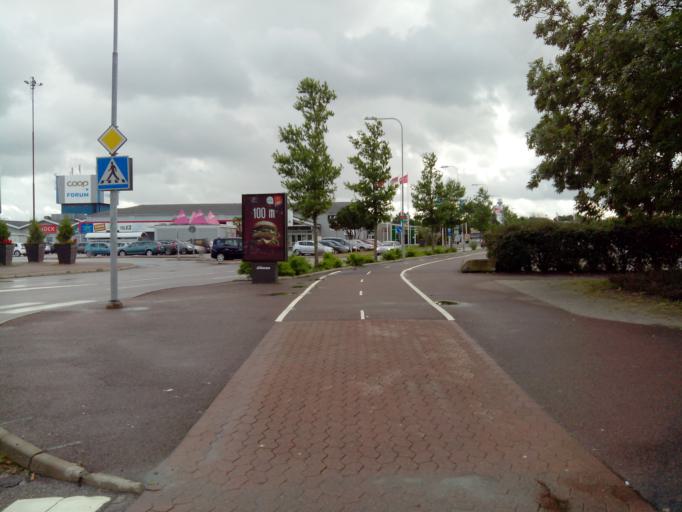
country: SE
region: Vaestra Goetaland
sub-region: Goteborg
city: Goeteborg
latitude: 57.7234
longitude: 11.9509
